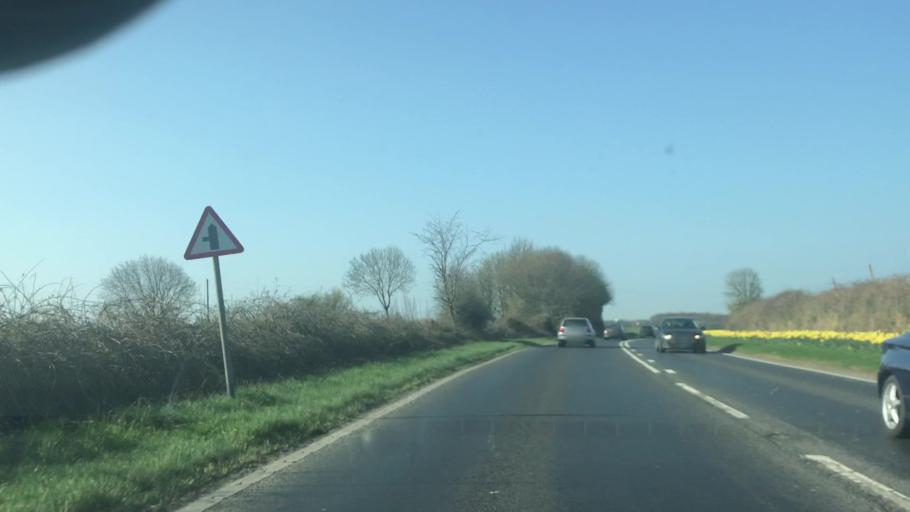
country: GB
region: England
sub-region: City and Borough of Leeds
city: Shadwell
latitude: 53.8775
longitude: -1.5087
